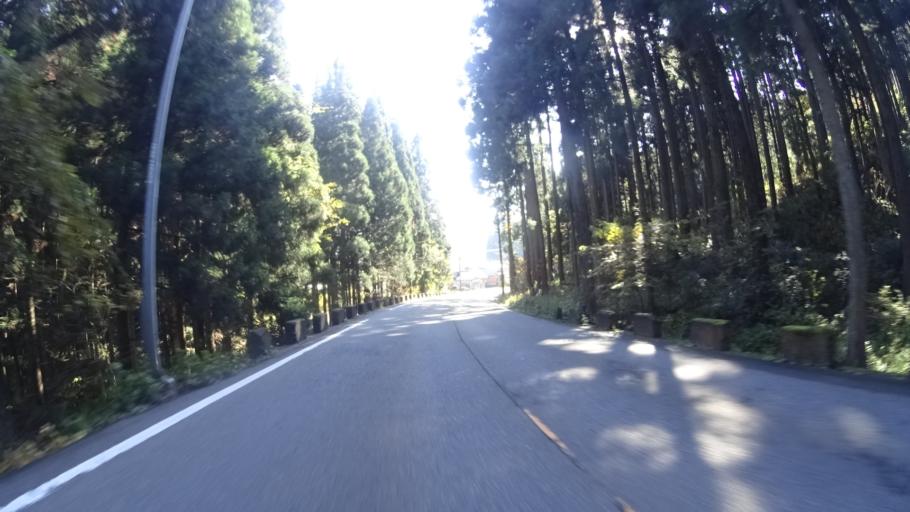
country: JP
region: Ishikawa
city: Tsurugi-asahimachi
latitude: 36.3657
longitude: 136.5906
